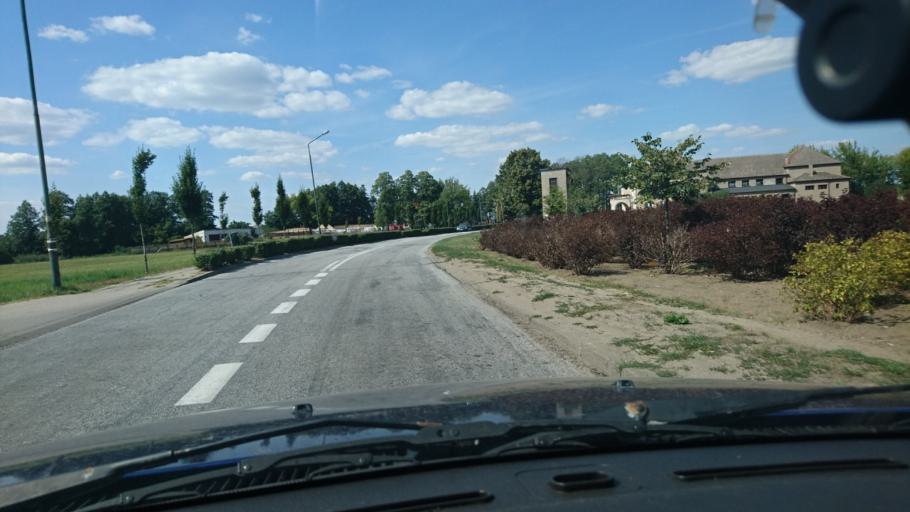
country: PL
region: Greater Poland Voivodeship
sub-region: Powiat krotoszynski
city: Sulmierzyce
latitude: 51.6071
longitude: 17.5250
